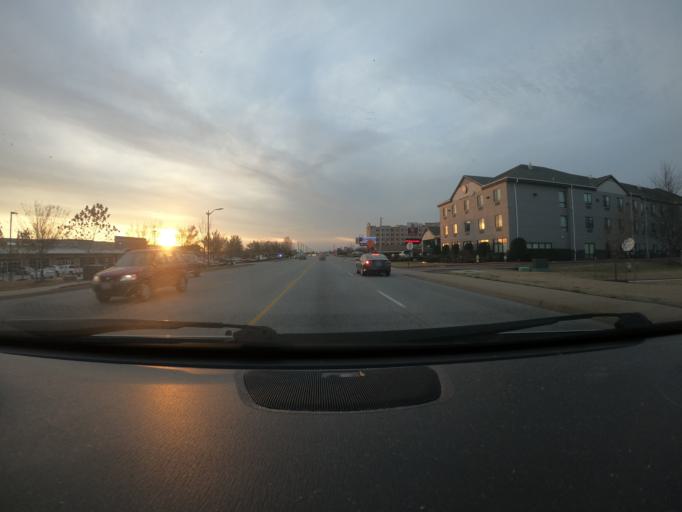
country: US
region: Arkansas
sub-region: Benton County
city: Bentonville
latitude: 36.3355
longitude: -94.2036
